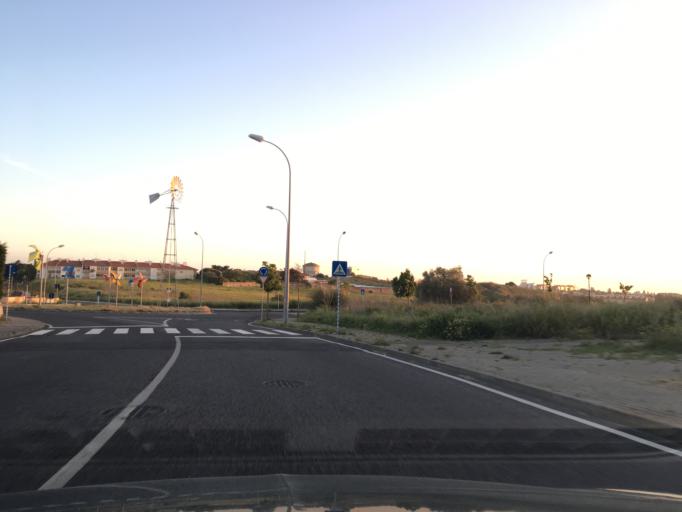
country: PT
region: Lisbon
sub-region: Oeiras
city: Terrugem
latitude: 38.7077
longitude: -9.2873
